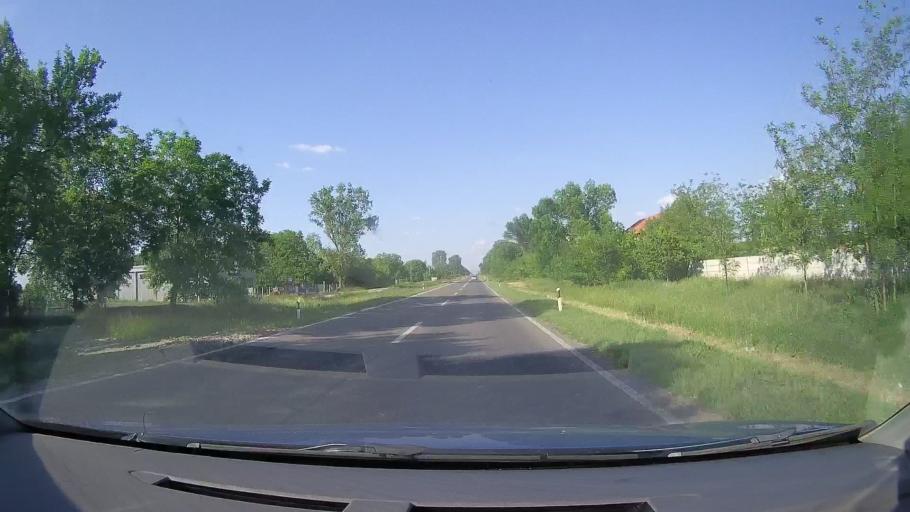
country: RS
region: Autonomna Pokrajina Vojvodina
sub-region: Juznobanatski Okrug
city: Pancevo
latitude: 44.9108
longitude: 20.6972
